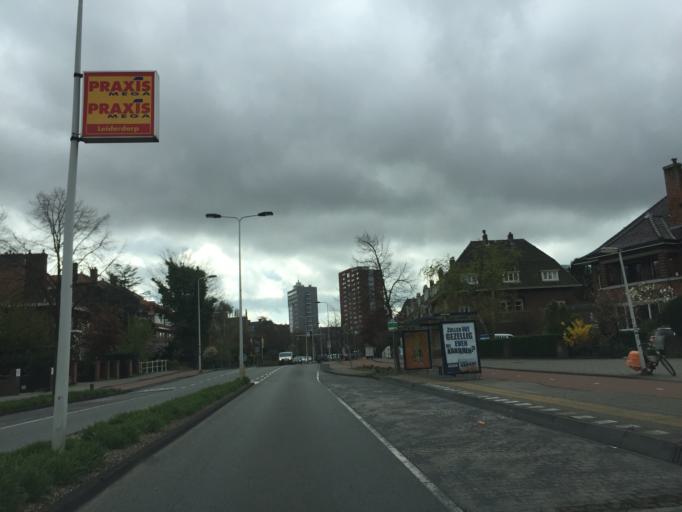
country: NL
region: South Holland
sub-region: Gemeente Oegstgeest
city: Oegstgeest
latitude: 52.1703
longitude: 4.4798
